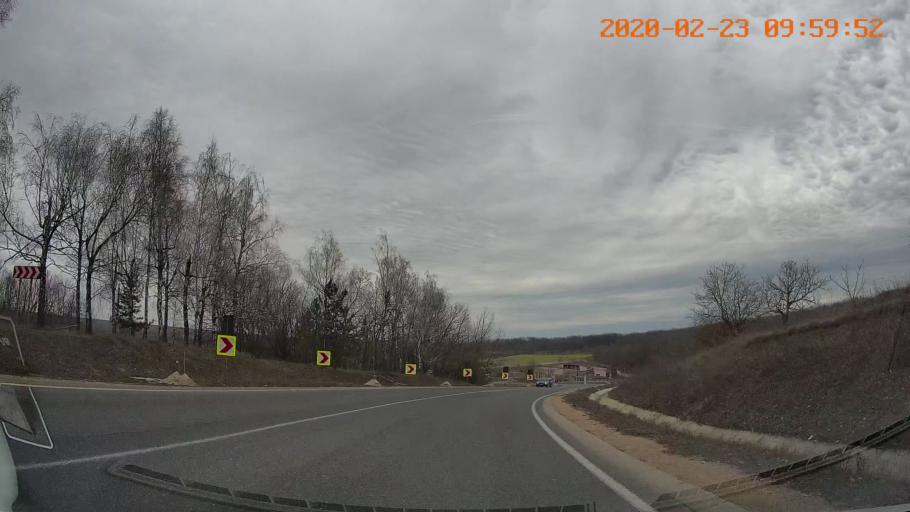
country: MD
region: Rezina
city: Saharna
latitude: 47.5973
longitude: 28.8275
